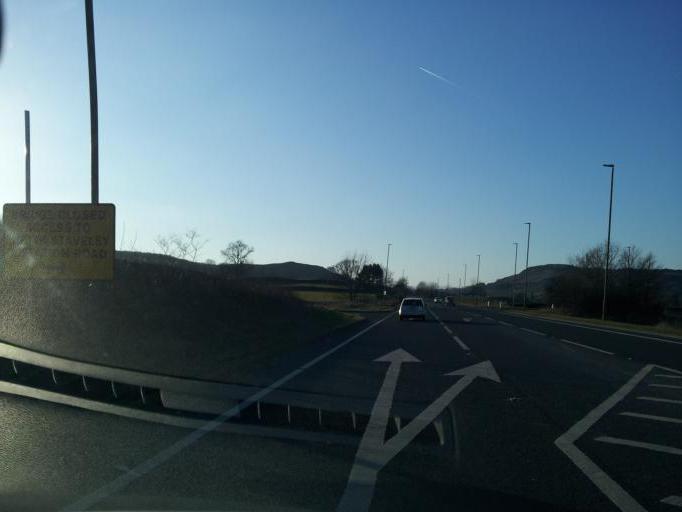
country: GB
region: England
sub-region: Cumbria
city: Kendal
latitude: 54.3681
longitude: -2.8054
